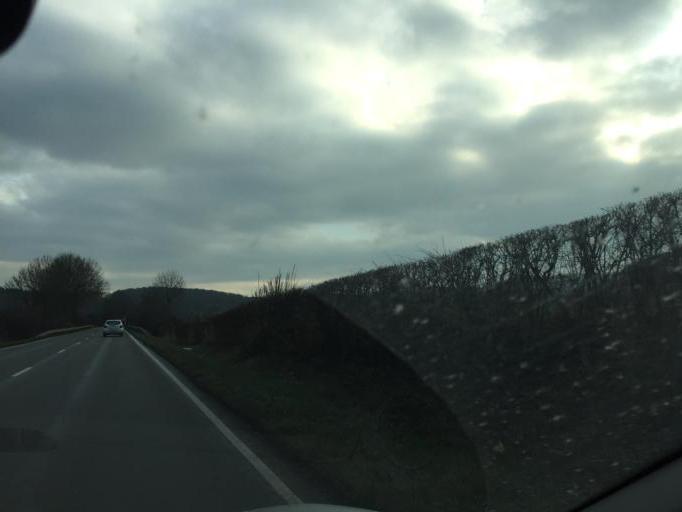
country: LU
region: Diekirch
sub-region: Canton de Redange
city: Useldange
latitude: 49.7517
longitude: 5.9678
